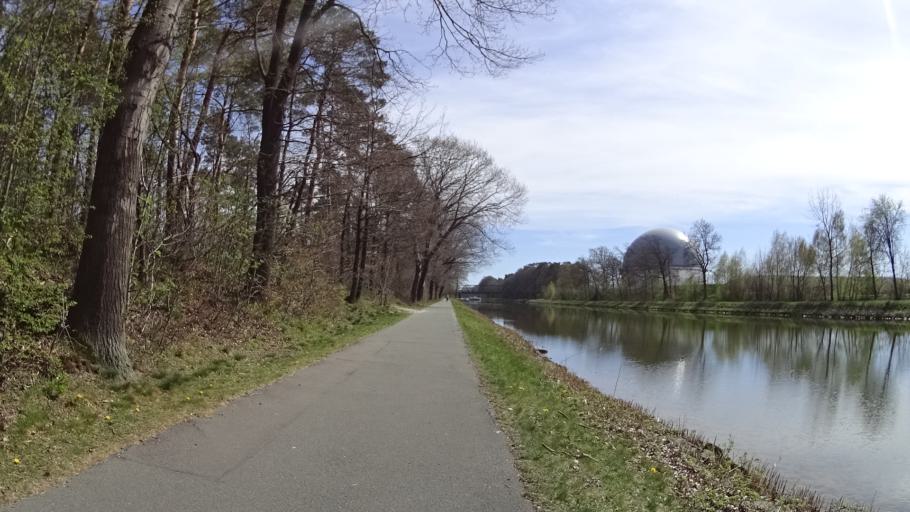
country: DE
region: North Rhine-Westphalia
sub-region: Regierungsbezirk Munster
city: Rheine
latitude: 52.3233
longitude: 7.4562
